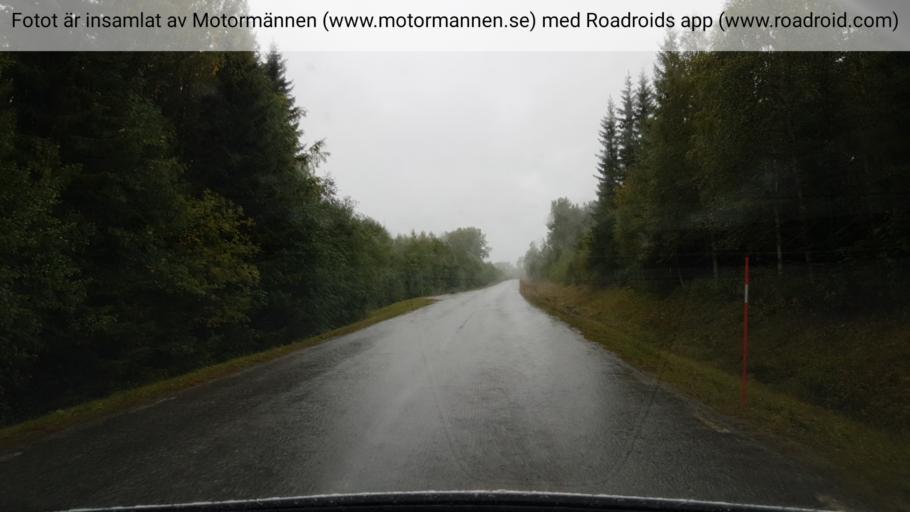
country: SE
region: Vaesterbotten
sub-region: Vannas Kommun
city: Vannasby
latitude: 64.0600
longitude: 19.9347
